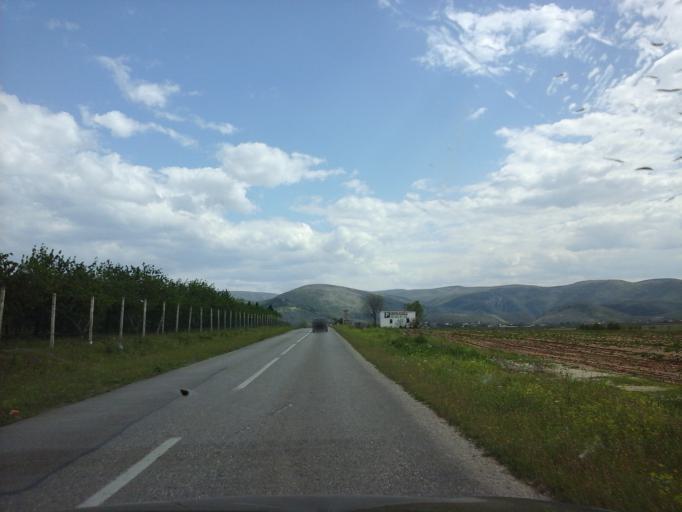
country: BA
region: Federation of Bosnia and Herzegovina
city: Blagaj
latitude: 43.2733
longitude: 17.8576
